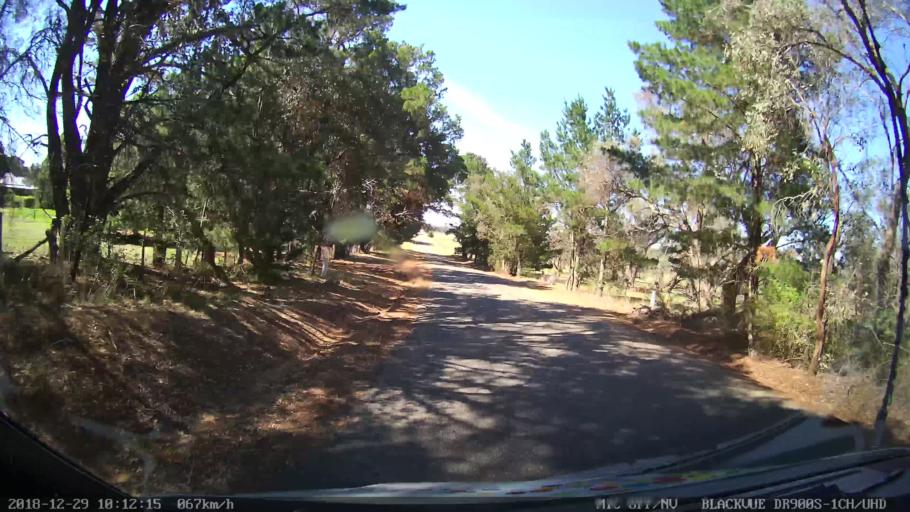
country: AU
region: New South Wales
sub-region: Yass Valley
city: Gundaroo
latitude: -34.8918
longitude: 149.4490
